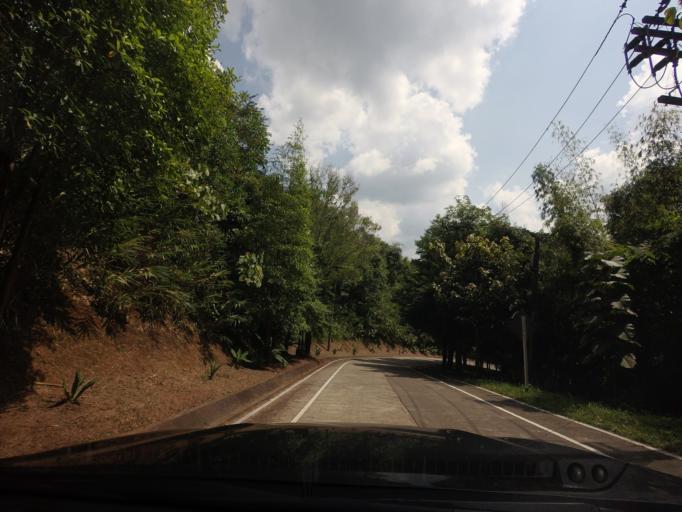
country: TH
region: Nan
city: Bo Kluea
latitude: 19.0197
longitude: 101.2089
